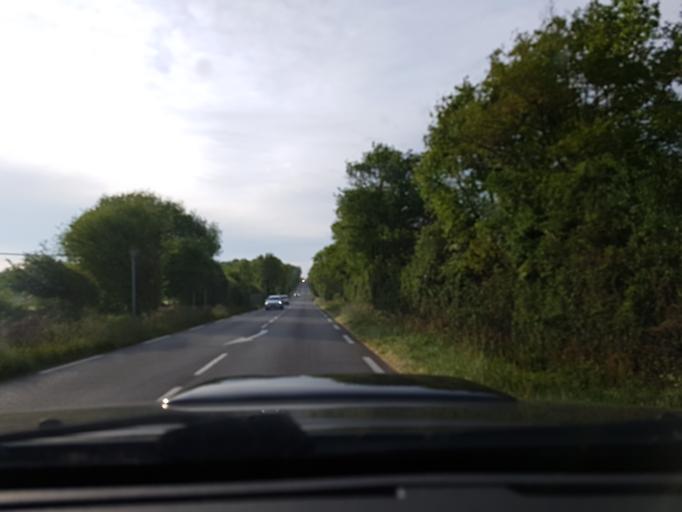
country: FR
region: Pays de la Loire
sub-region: Departement de la Vendee
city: Aizenay
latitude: 46.7560
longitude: -1.6391
